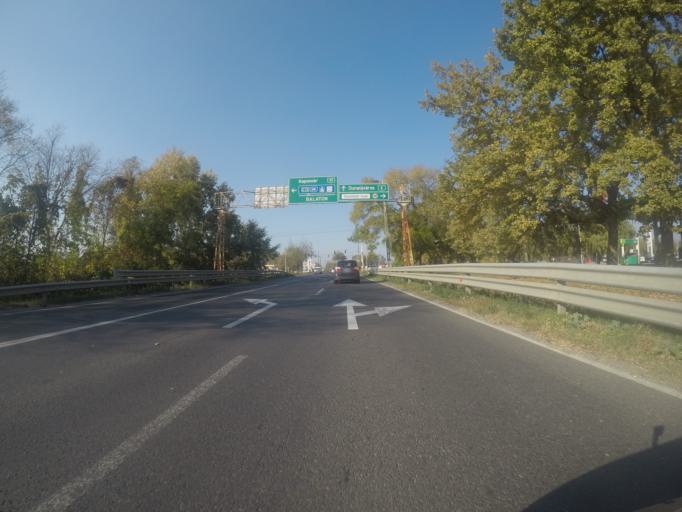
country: HU
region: Tolna
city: Dunafoldvar
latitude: 46.8123
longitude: 18.9099
